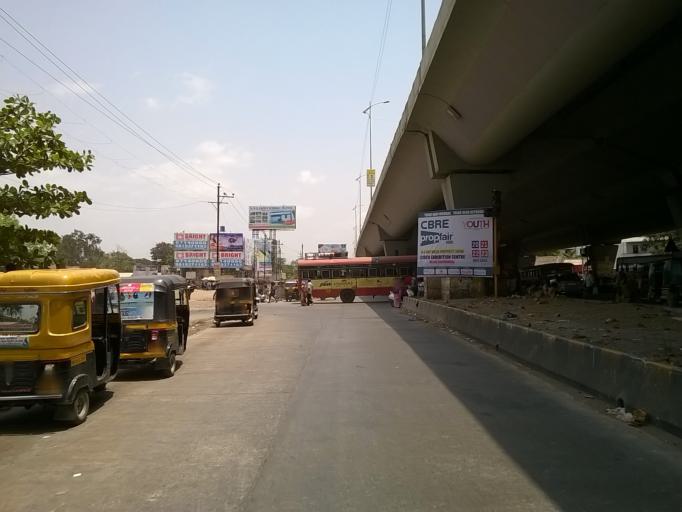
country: IN
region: Maharashtra
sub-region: Raigarh
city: Panvel
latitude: 18.9915
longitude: 73.1158
